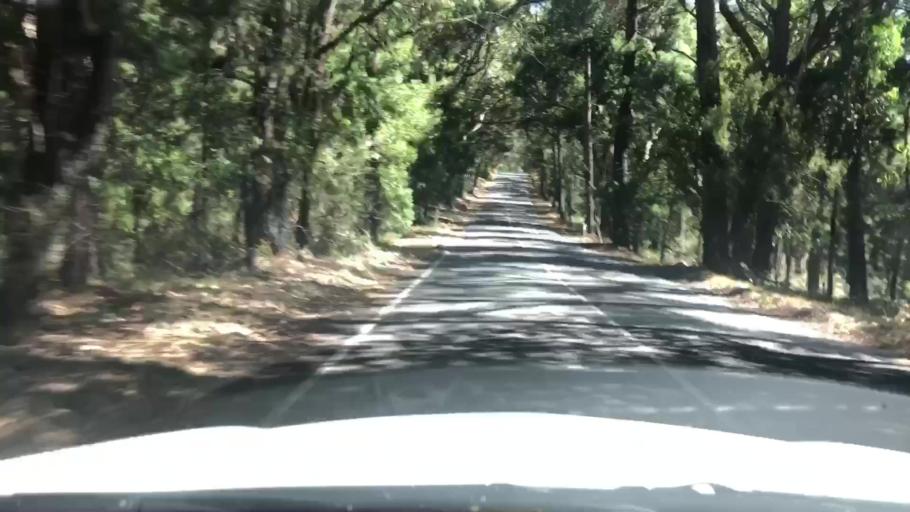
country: AU
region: Victoria
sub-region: Yarra Ranges
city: Macclesfield
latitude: -37.8588
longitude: 145.4800
